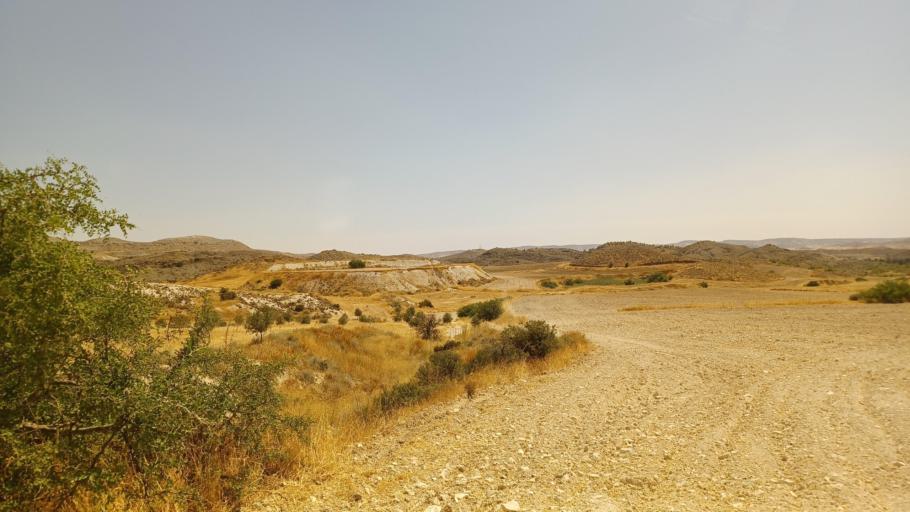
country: CY
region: Larnaka
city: Athienou
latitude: 35.0037
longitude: 33.5547
